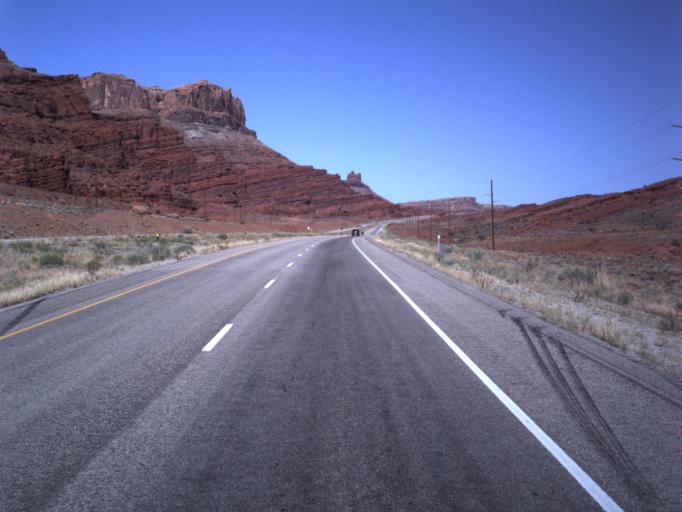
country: US
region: Utah
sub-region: Grand County
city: Moab
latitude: 38.6236
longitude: -109.6463
